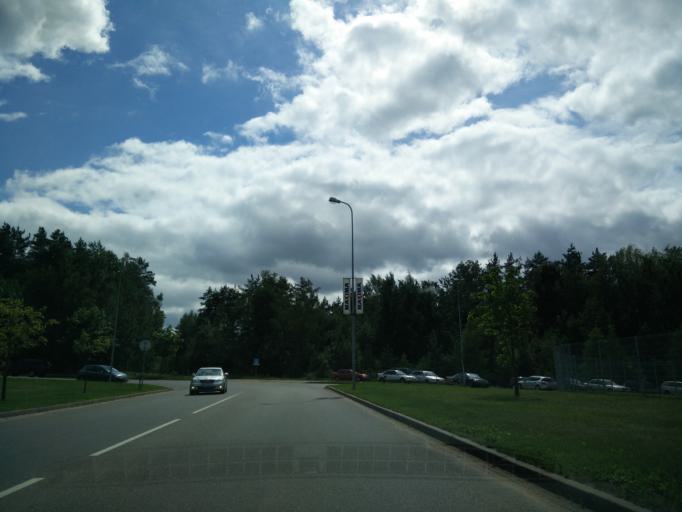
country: LT
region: Vilnius County
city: Pilaite
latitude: 54.6552
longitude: 25.1411
